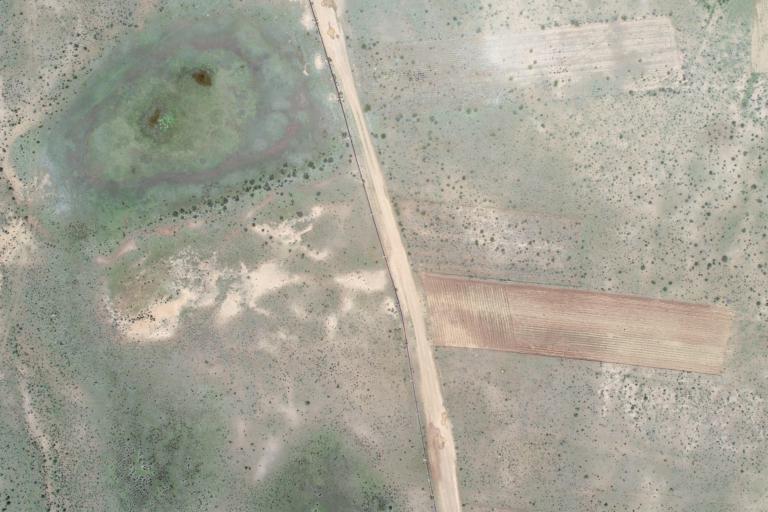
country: BO
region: La Paz
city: Patacamaya
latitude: -17.2780
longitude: -68.5133
